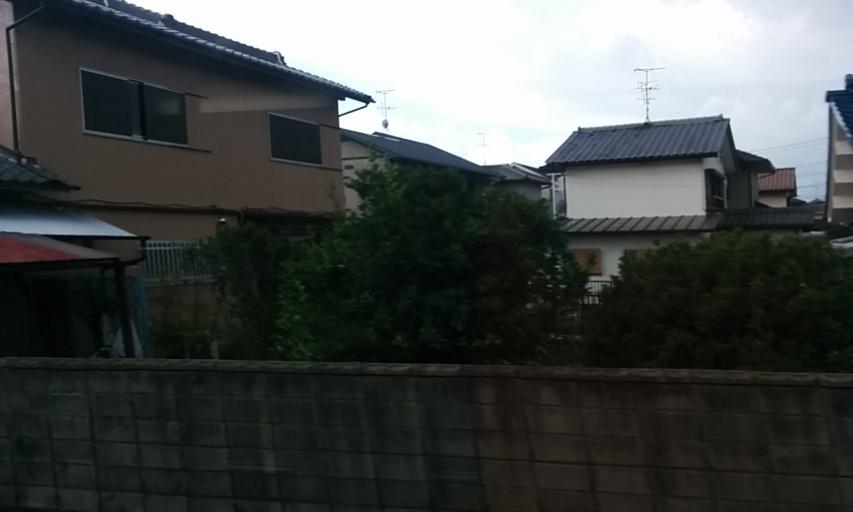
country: JP
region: Nara
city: Tawaramoto
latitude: 34.5609
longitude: 135.7883
